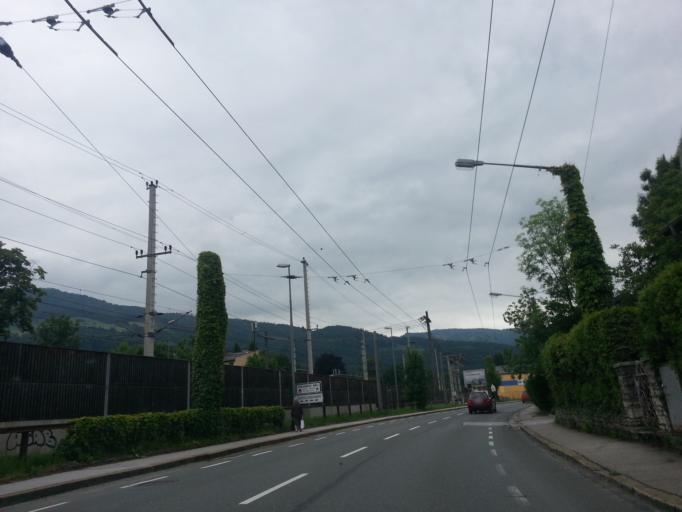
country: AT
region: Salzburg
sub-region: Salzburg Stadt
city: Salzburg
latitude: 47.7881
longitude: 13.0789
